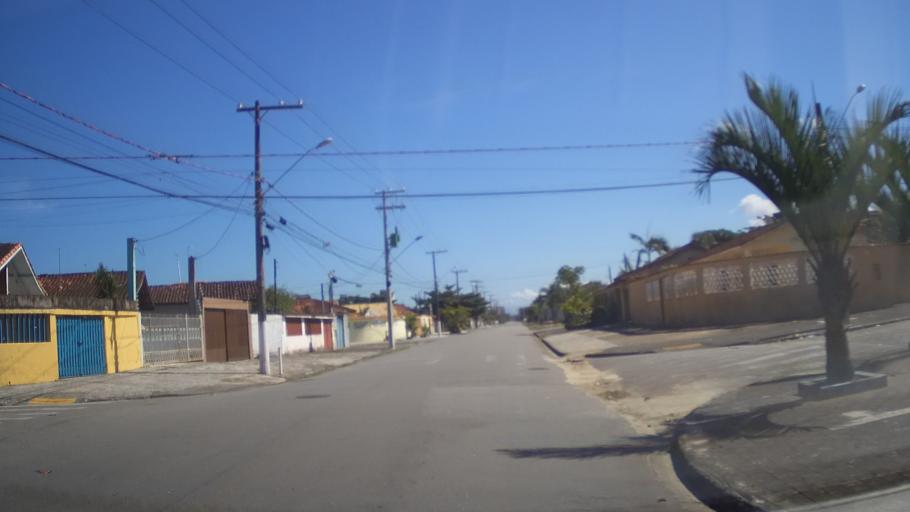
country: BR
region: Sao Paulo
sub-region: Mongagua
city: Mongagua
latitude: -24.1252
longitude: -46.6798
